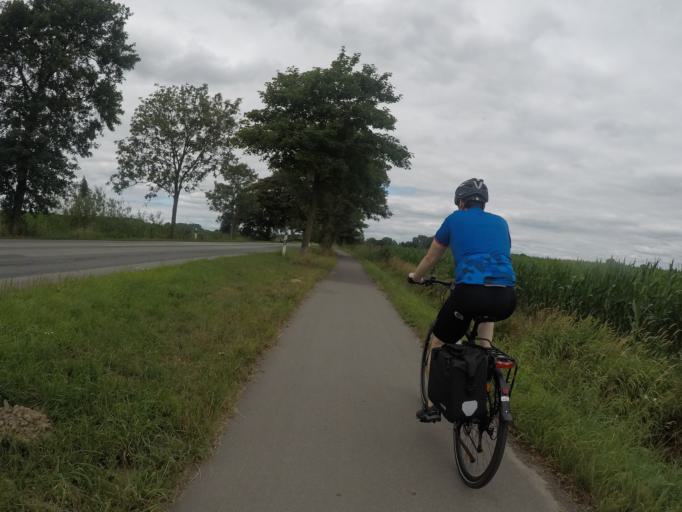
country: DE
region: Lower Saxony
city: Himmelpforten
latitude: 53.6420
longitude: 9.2972
